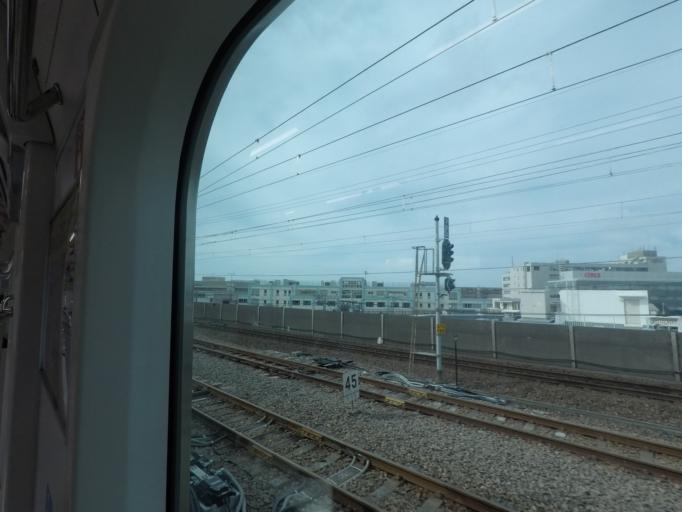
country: JP
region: Kanagawa
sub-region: Kawasaki-shi
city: Kawasaki
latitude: 35.5803
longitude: 139.6430
